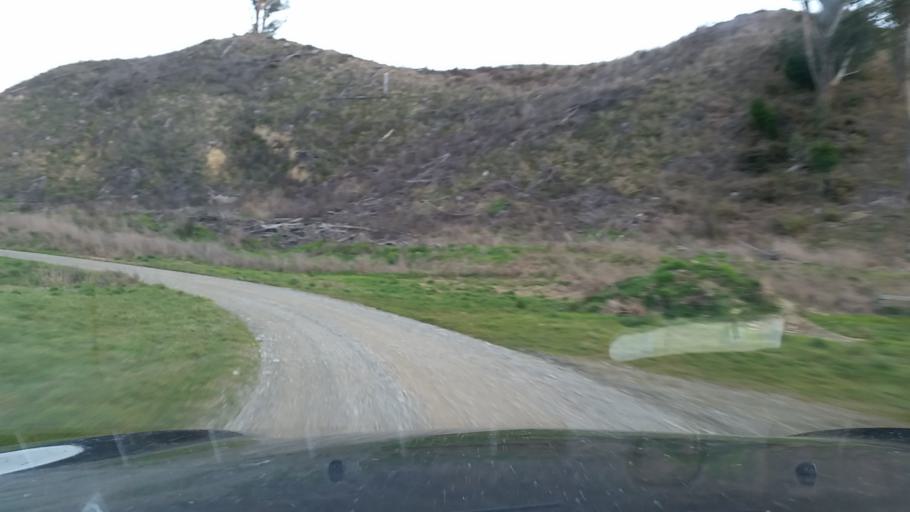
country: NZ
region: Marlborough
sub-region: Marlborough District
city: Blenheim
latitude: -41.5092
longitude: 173.5907
